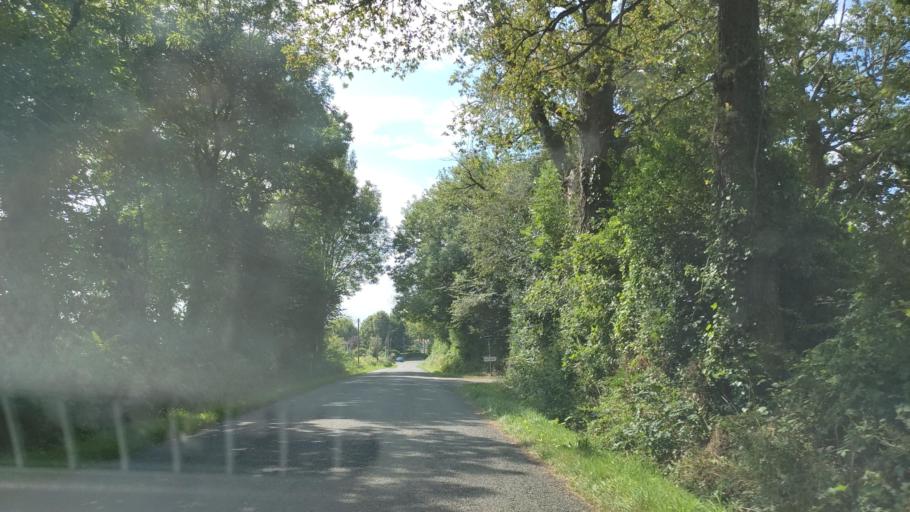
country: FR
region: Limousin
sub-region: Departement de la Haute-Vienne
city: Couzeix
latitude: 45.8503
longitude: 1.1924
